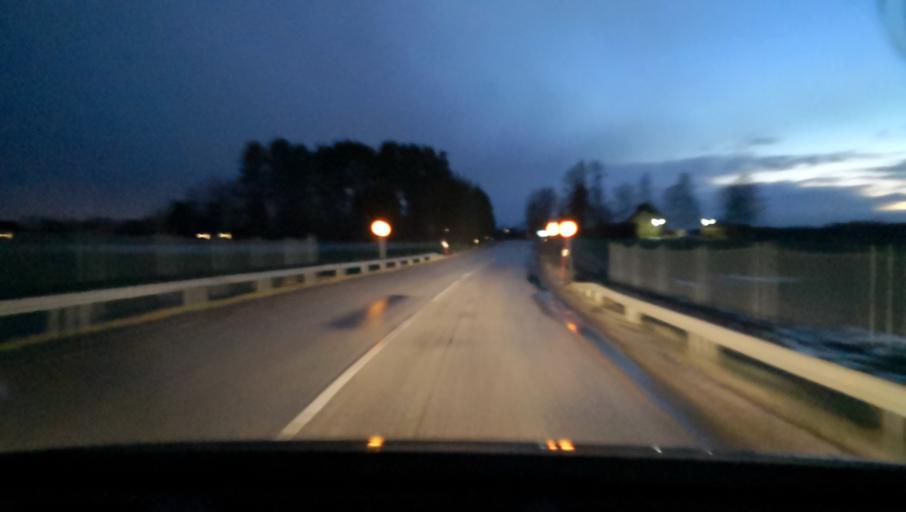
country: SE
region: Vaestmanland
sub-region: Vasteras
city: Skultuna
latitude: 59.7771
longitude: 16.4625
